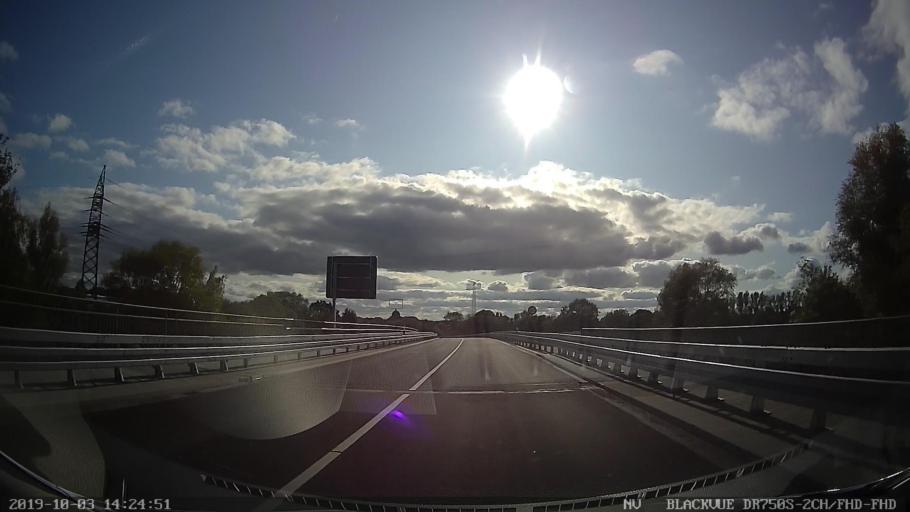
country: DE
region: Schleswig-Holstein
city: Pinneberg
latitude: 53.6670
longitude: 9.7773
